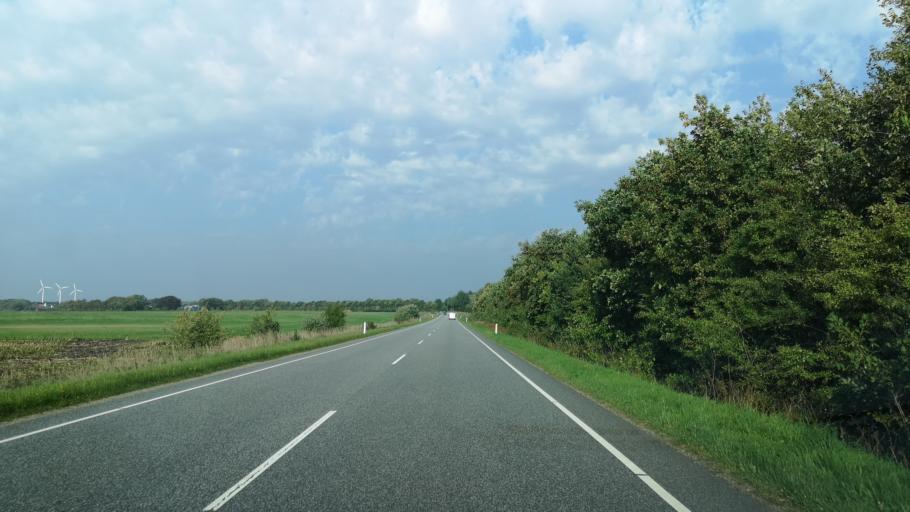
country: DK
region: Central Jutland
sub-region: Herning Kommune
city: Kibaek
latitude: 55.9783
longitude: 8.8286
